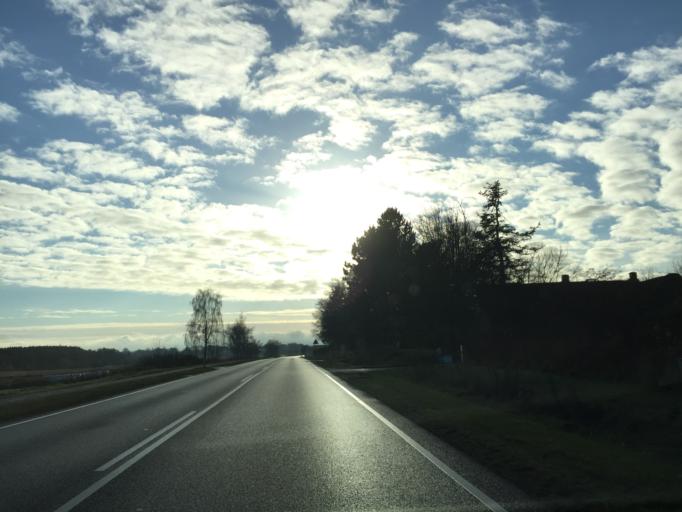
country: DK
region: Central Jutland
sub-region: Arhus Kommune
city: Sabro
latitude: 56.1995
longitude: 10.0152
